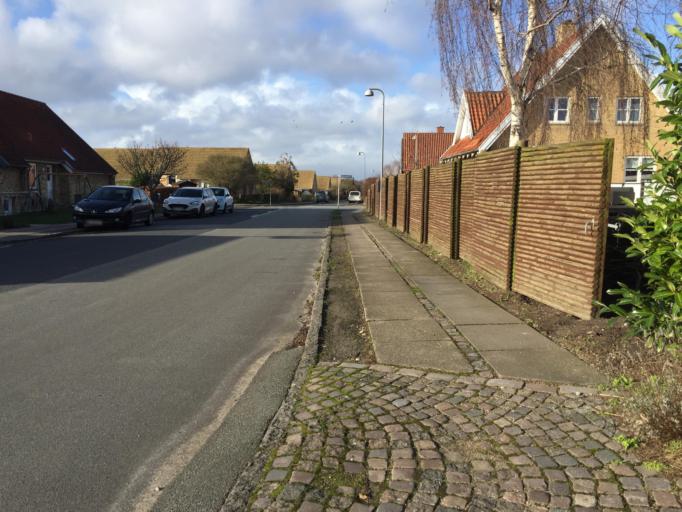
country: DK
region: South Denmark
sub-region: Odense Kommune
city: Odense
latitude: 55.3833
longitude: 10.4152
